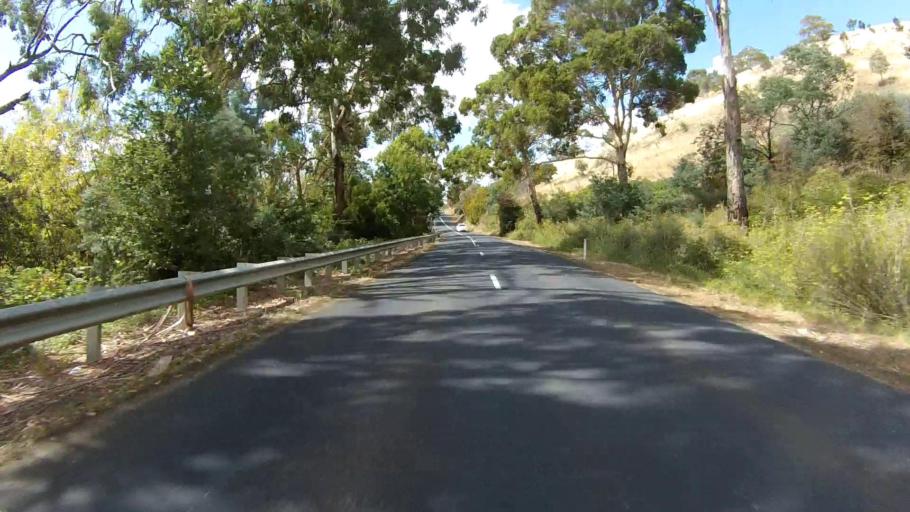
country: AU
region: Tasmania
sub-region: Derwent Valley
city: New Norfolk
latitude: -42.7317
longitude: 146.9039
